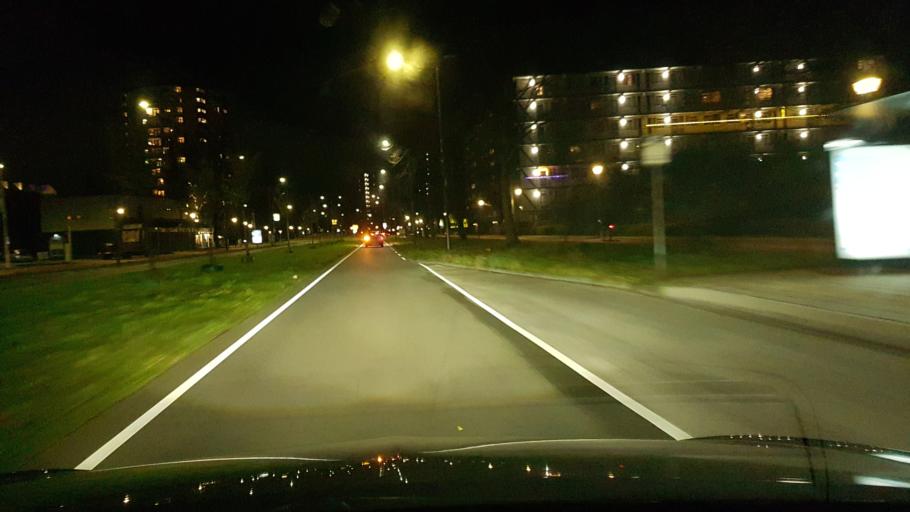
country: NL
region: North Holland
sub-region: Gemeente Haarlem
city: Haarlem
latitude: 52.3587
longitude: 4.6525
